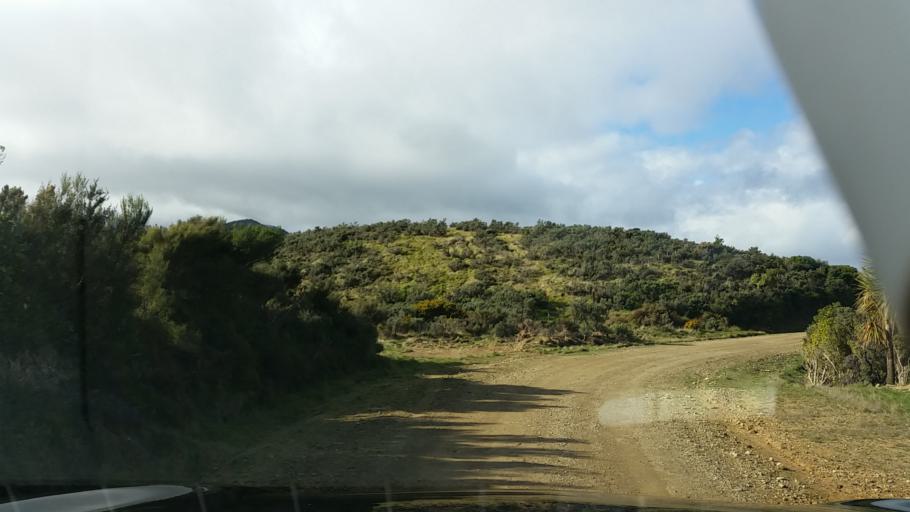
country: NZ
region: Marlborough
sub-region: Marlborough District
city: Picton
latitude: -40.9672
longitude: 173.8928
